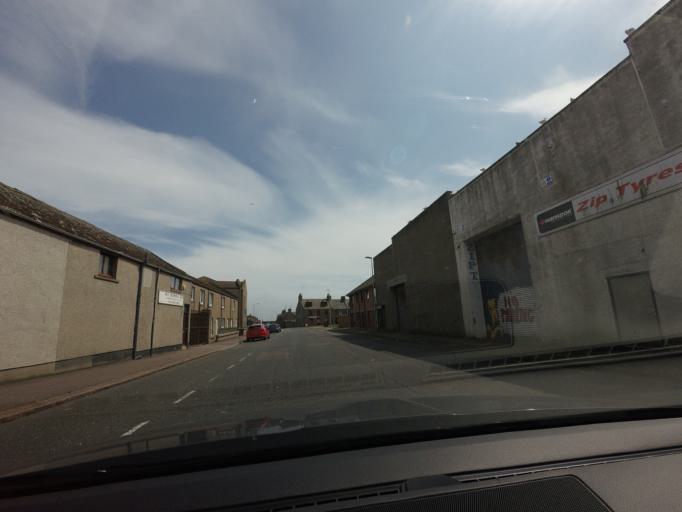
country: GB
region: Scotland
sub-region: Aberdeenshire
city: Peterhead
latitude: 57.5095
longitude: -1.7788
